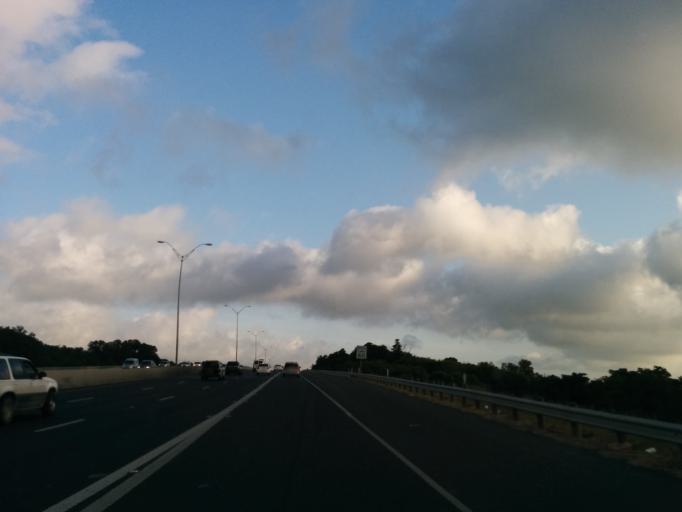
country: US
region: Texas
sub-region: Bexar County
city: Olmos Park
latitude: 29.4692
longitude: -98.4750
